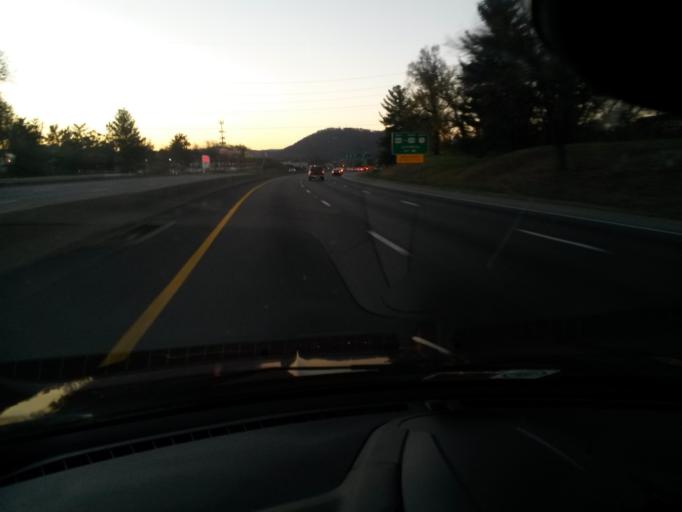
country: US
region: Virginia
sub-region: City of Roanoke
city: Roanoke
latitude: 37.2872
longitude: -79.9391
